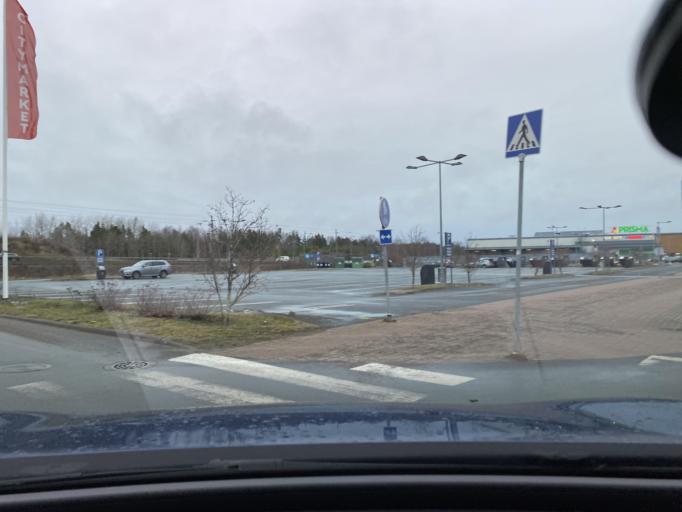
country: FI
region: Satakunta
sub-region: Rauma
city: Rauma
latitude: 61.1326
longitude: 21.5103
